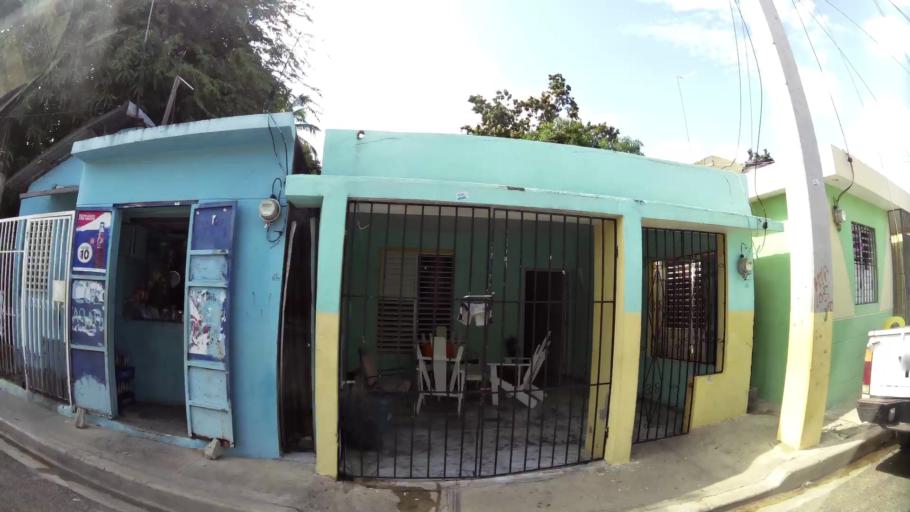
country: DO
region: La Vega
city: Concepcion de La Vega
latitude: 19.2215
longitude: -70.5360
